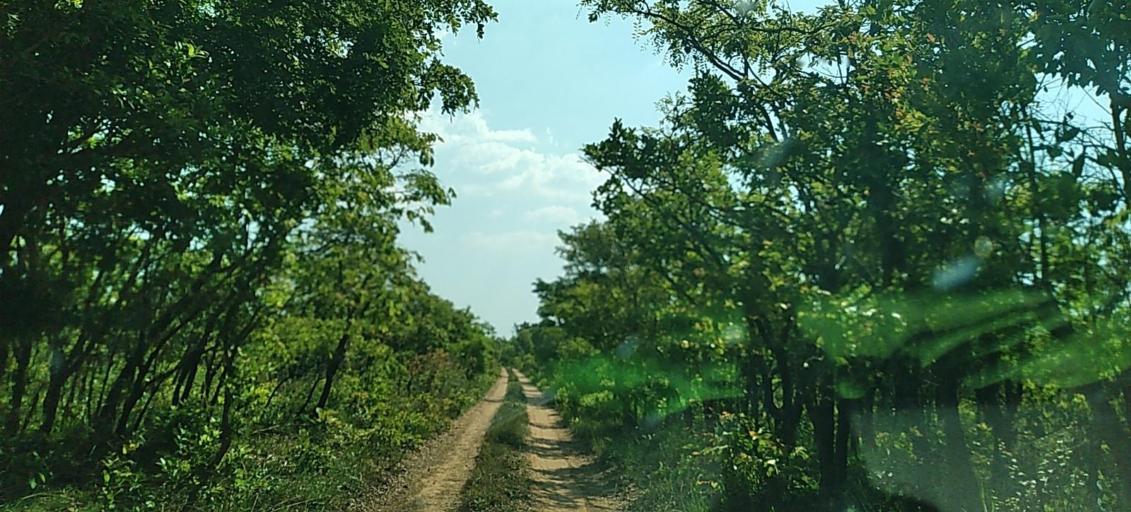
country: CD
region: Katanga
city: Kolwezi
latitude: -11.2699
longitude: 24.9928
